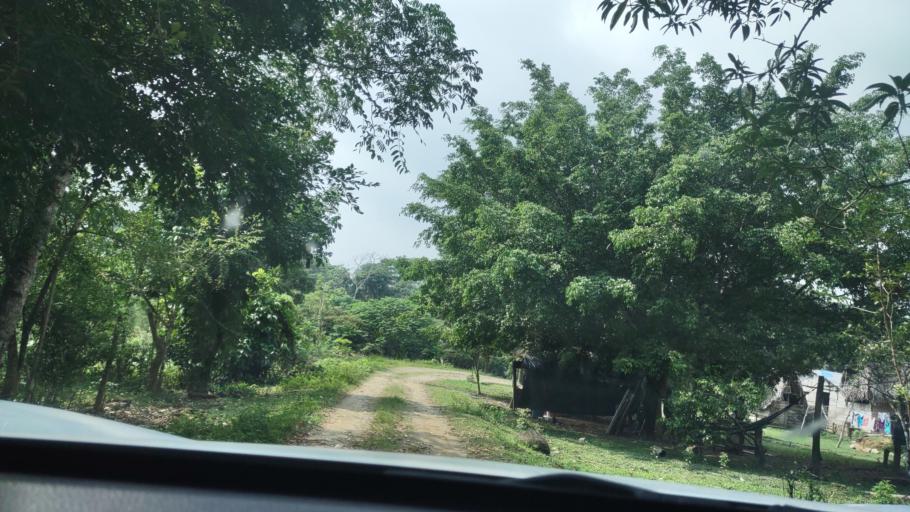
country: MX
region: Veracruz
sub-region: Uxpanapa
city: Poblado 10
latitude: 17.5454
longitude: -94.2931
